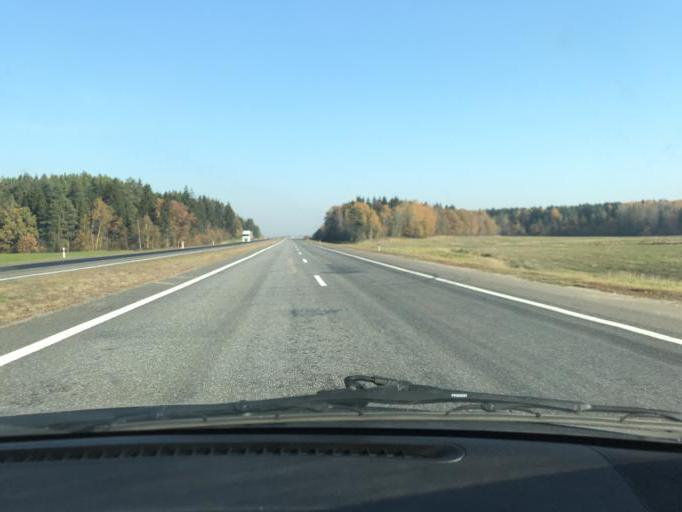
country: BY
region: Vitebsk
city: Horad Orsha
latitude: 54.5849
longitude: 30.3367
